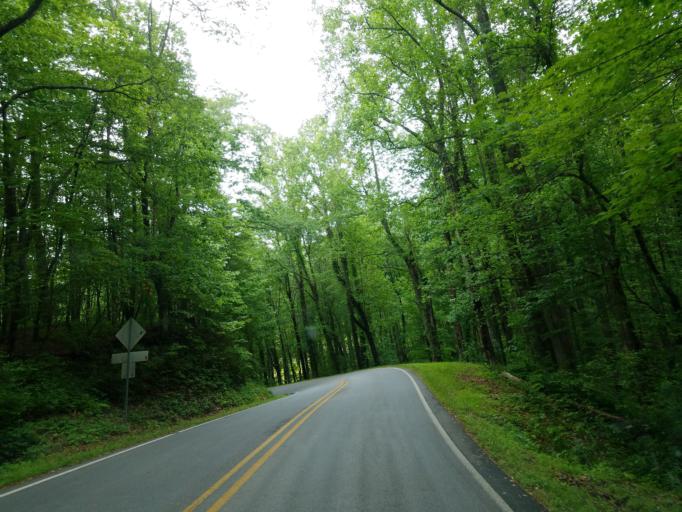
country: US
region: Georgia
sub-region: Union County
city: Blairsville
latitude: 34.7089
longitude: -83.9970
